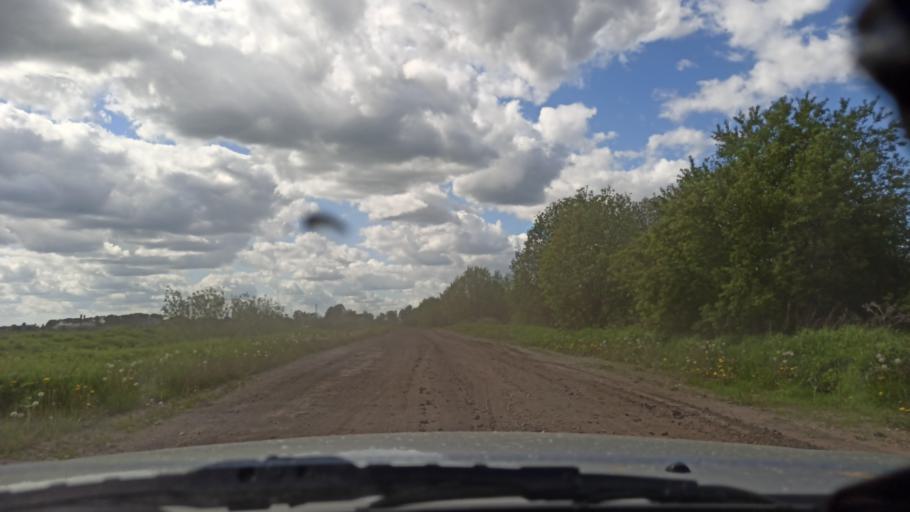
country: RU
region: Vologda
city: Vologda
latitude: 59.3411
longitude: 39.8381
